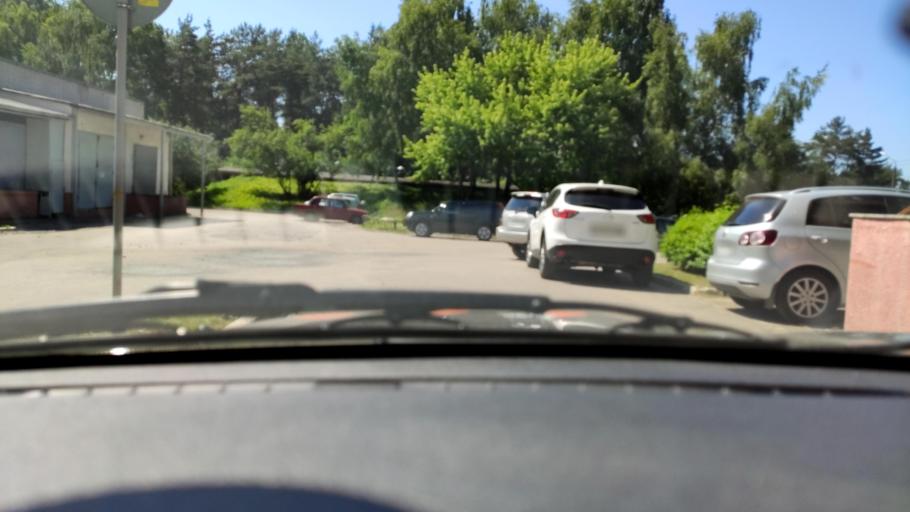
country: RU
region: Voronezj
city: Podgornoye
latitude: 51.7427
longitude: 39.1788
